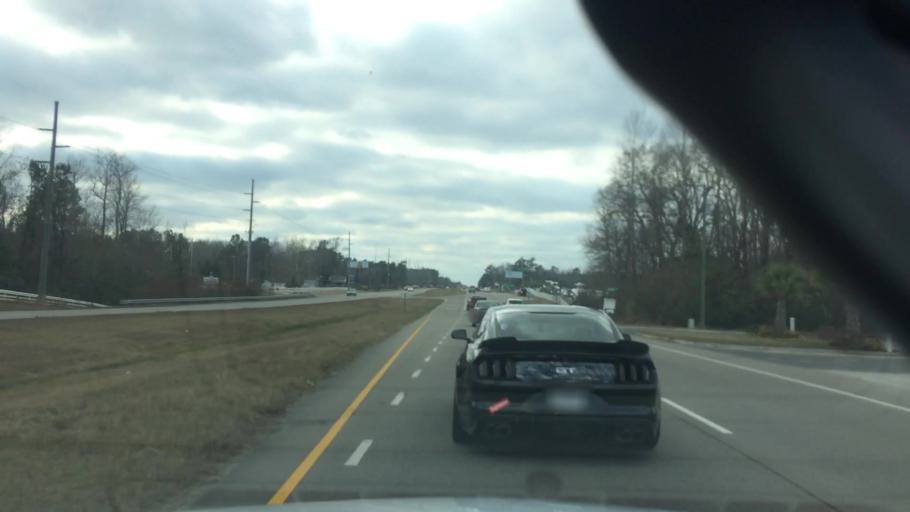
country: US
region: North Carolina
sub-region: Brunswick County
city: Shallotte
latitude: 34.0094
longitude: -78.2956
